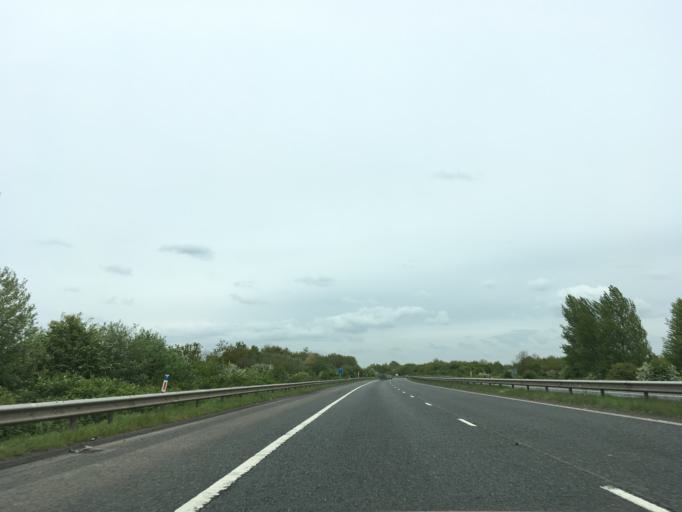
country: GB
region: England
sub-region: South Gloucestershire
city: Severn Beach
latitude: 51.5328
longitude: -2.6463
